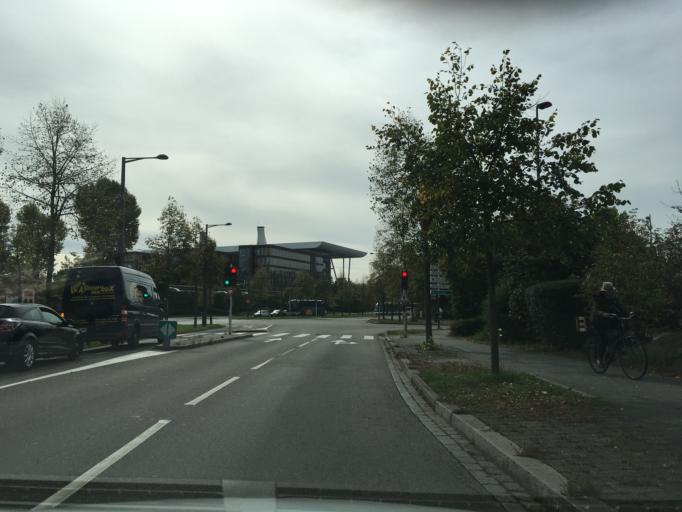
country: FR
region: Alsace
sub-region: Departement du Bas-Rhin
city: Schiltigheim
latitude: 48.5978
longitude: 7.7769
